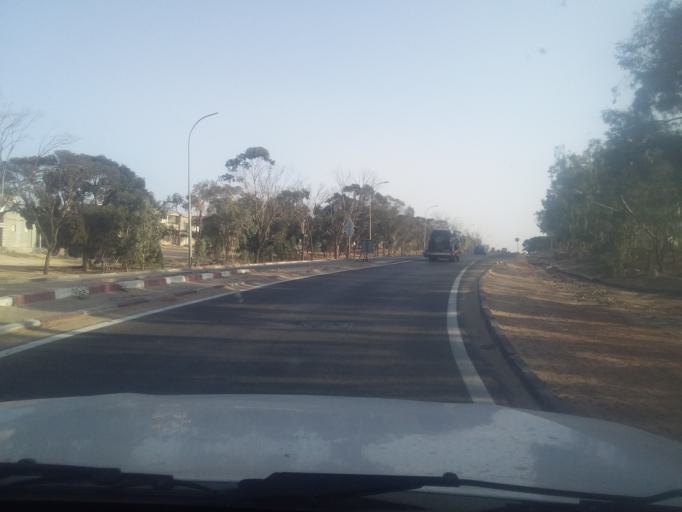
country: TN
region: Qabis
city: Gabes
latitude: 33.6350
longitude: 10.2821
